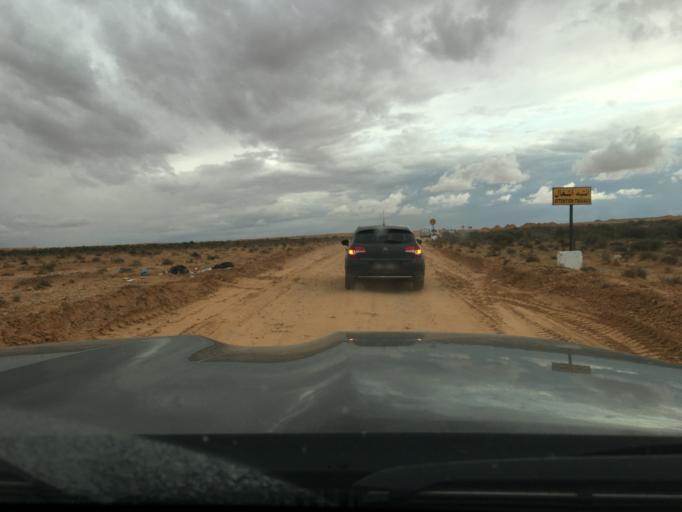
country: TN
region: Madanin
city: Medenine
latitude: 33.2612
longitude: 10.5728
